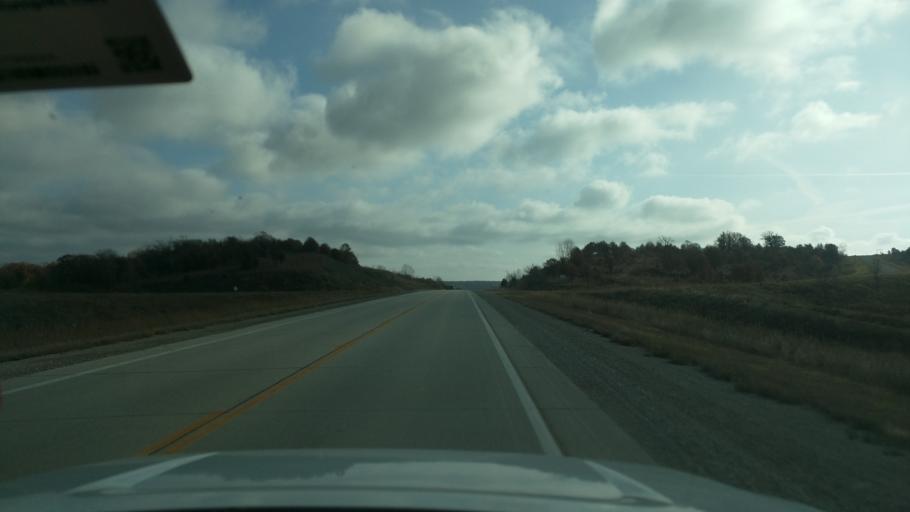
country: US
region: Kansas
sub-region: Chautauqua County
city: Sedan
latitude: 37.0822
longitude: -96.1173
